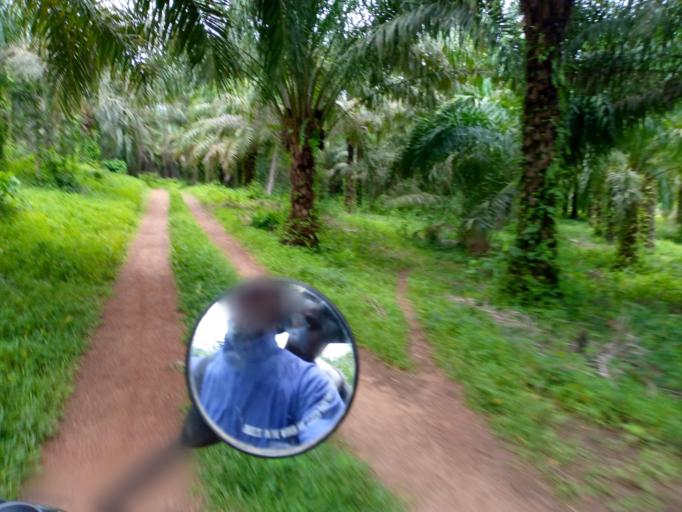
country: SL
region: Northern Province
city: Mange
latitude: 8.9874
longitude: -12.7212
